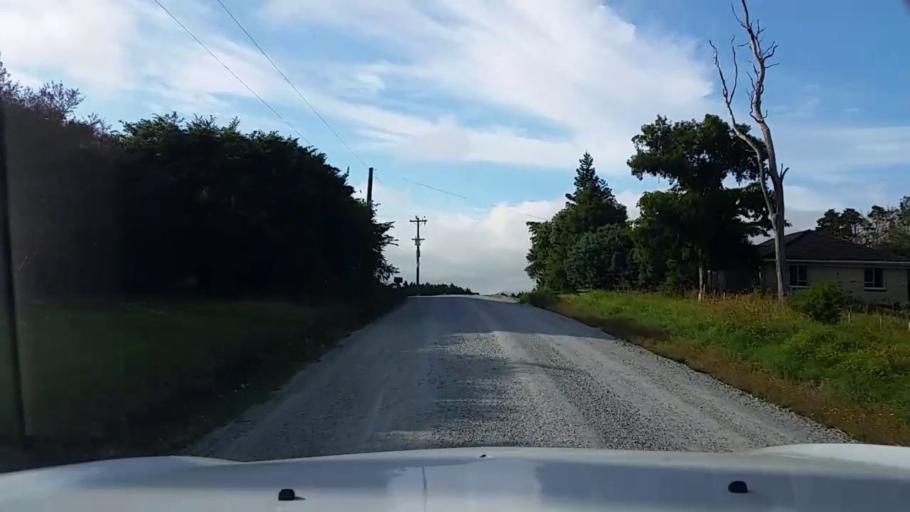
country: NZ
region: Northland
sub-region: Whangarei
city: Maungatapere
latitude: -35.6815
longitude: 174.1787
